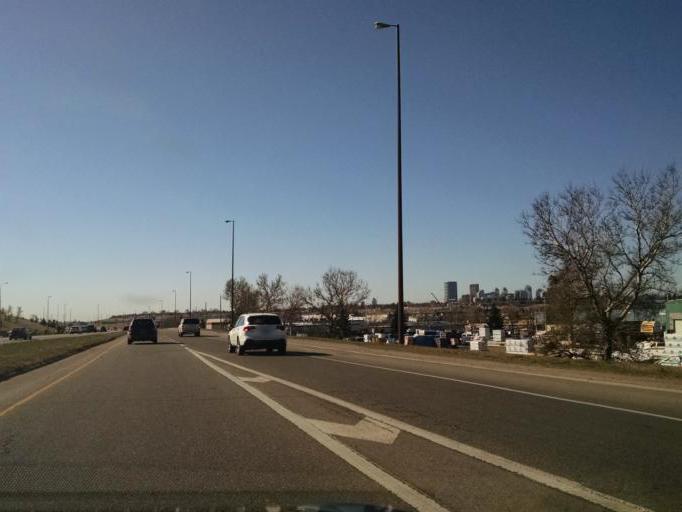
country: CA
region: Alberta
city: Calgary
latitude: 51.0931
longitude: -114.0402
